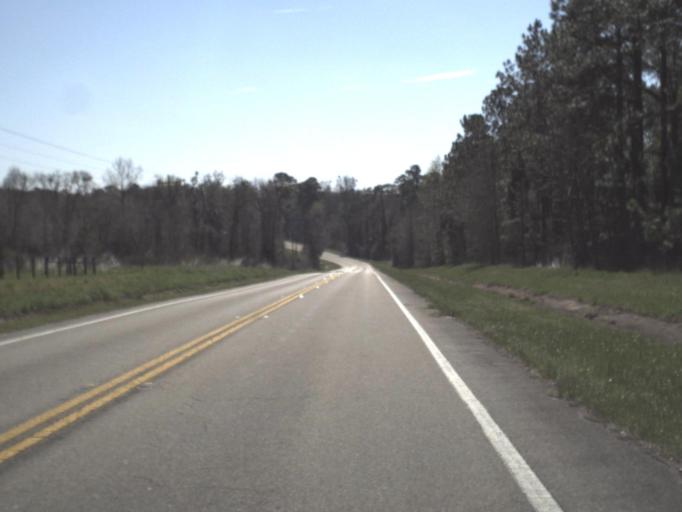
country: US
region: Florida
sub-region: Jefferson County
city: Monticello
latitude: 30.3786
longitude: -84.0043
